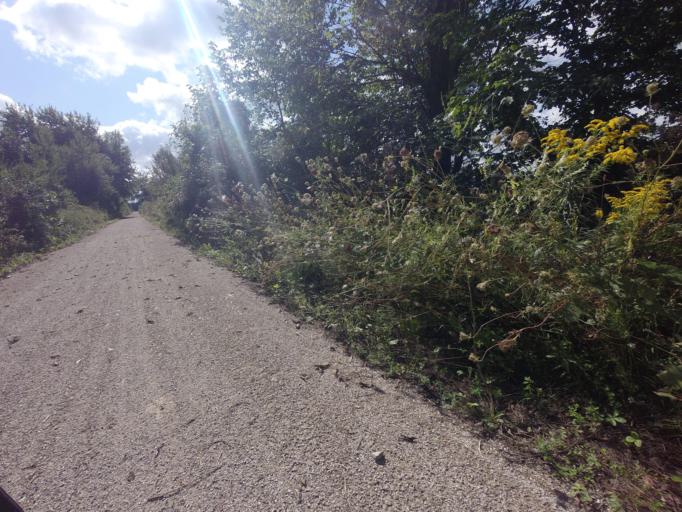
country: CA
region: Ontario
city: Huron East
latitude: 43.7160
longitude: -81.3865
